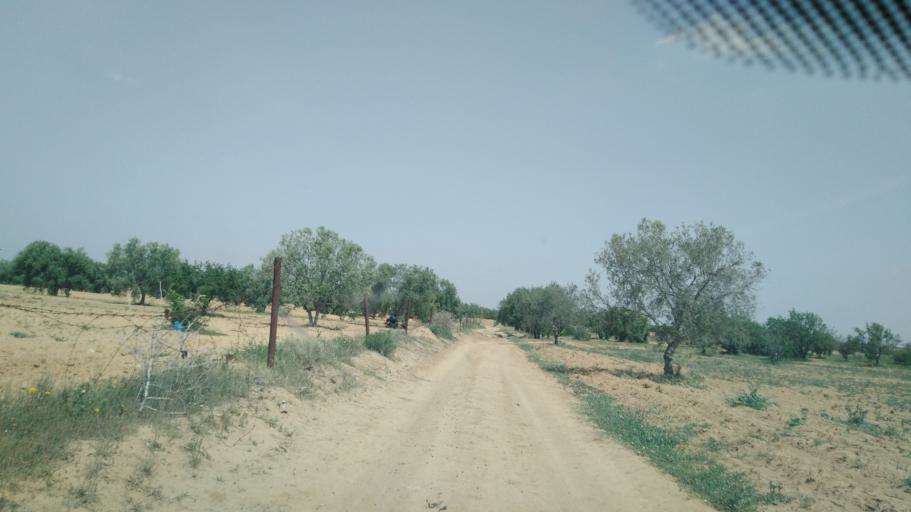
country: TN
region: Safaqis
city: Sfax
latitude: 34.7329
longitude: 10.5746
